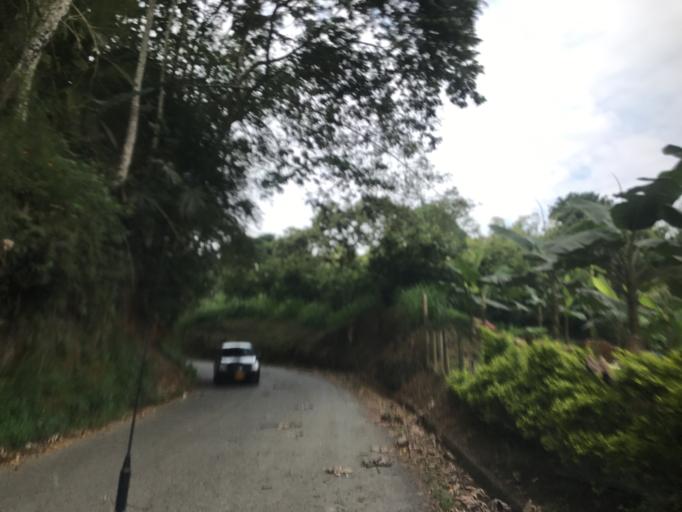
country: CO
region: Quindio
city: Montenegro
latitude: 4.5489
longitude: -75.8018
